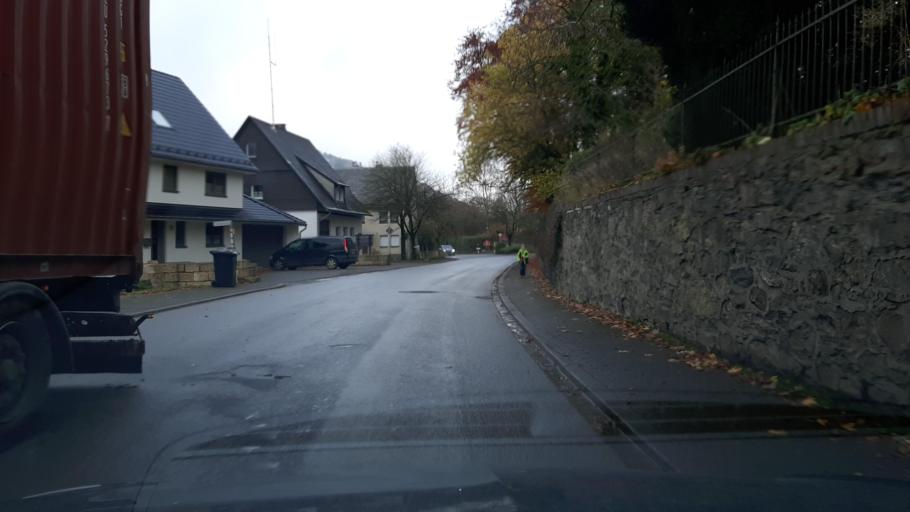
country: DE
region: North Rhine-Westphalia
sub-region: Regierungsbezirk Arnsberg
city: Olsberg
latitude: 51.3202
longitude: 8.5295
